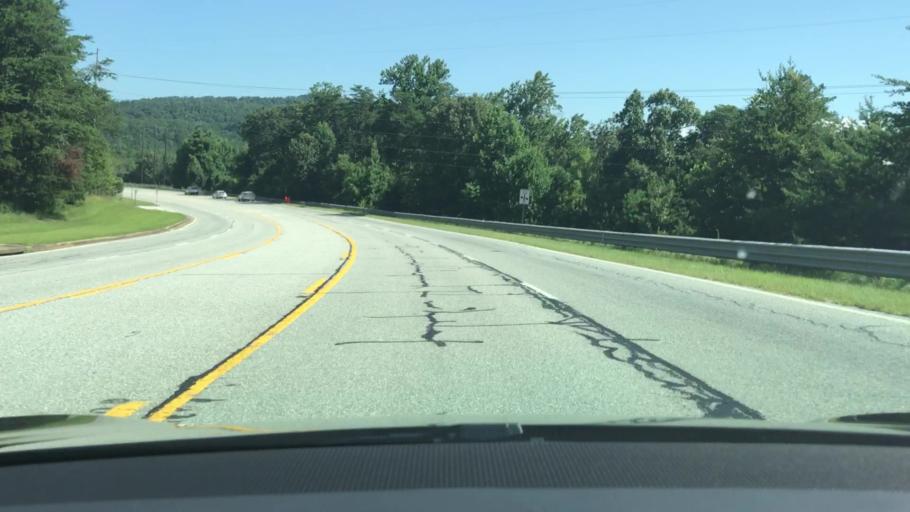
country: US
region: Georgia
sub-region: Rabun County
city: Clayton
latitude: 34.7324
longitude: -83.3889
